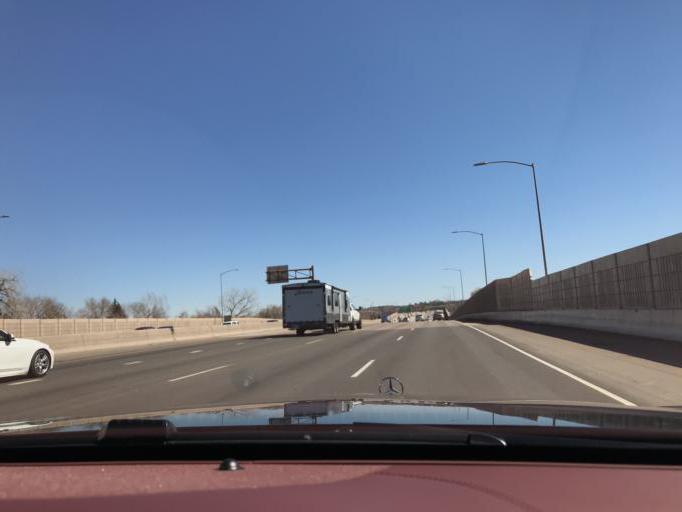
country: US
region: Colorado
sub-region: Jefferson County
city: Arvada
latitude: 39.7835
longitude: -105.1003
